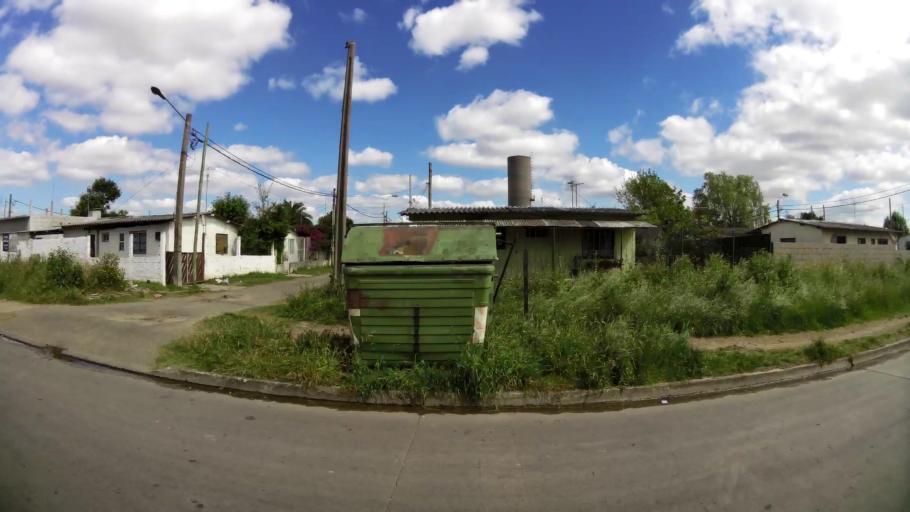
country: UY
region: Canelones
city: Paso de Carrasco
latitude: -34.8609
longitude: -56.1148
